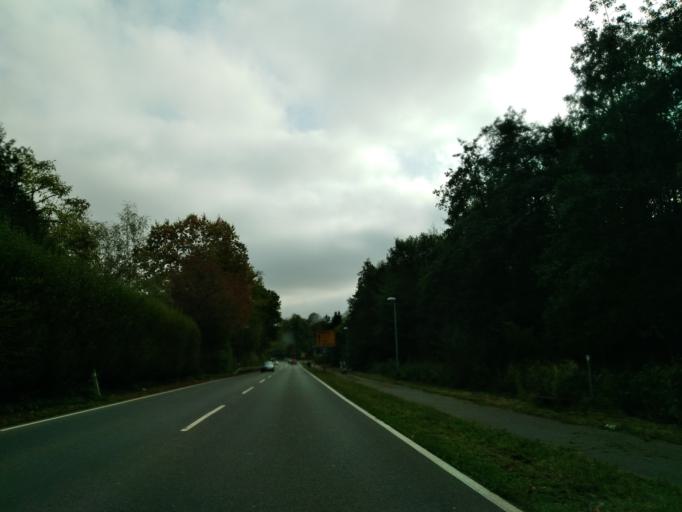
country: DE
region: North Rhine-Westphalia
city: Sankt Augustin
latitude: 50.7507
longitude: 7.2201
